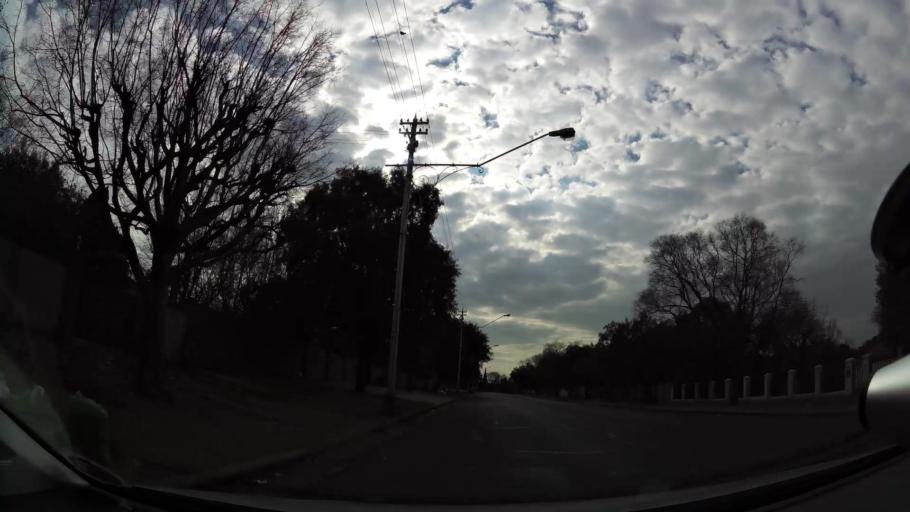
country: ZA
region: Orange Free State
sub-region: Mangaung Metropolitan Municipality
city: Bloemfontein
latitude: -29.0941
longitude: 26.2448
